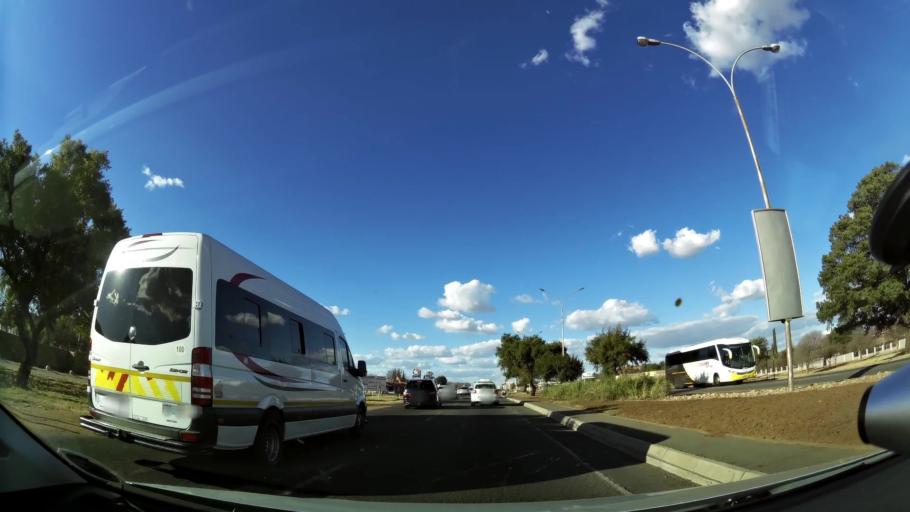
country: ZA
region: North-West
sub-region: Dr Kenneth Kaunda District Municipality
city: Klerksdorp
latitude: -26.8552
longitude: 26.6794
